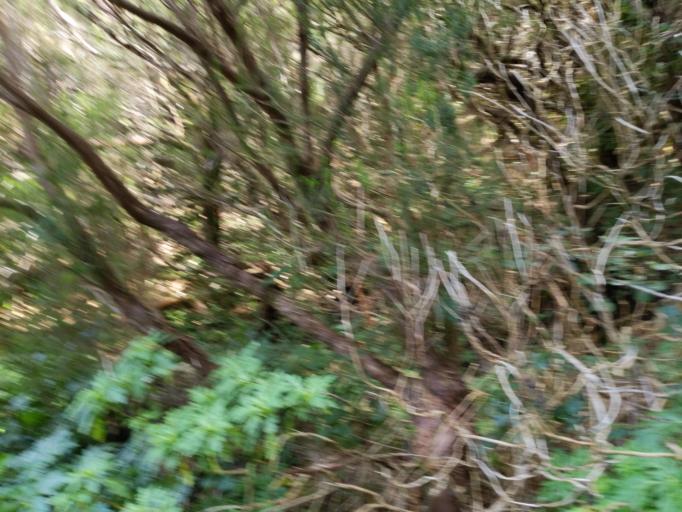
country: PT
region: Madeira
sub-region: Calheta
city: Arco da Calheta
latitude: 32.7621
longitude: -17.1259
